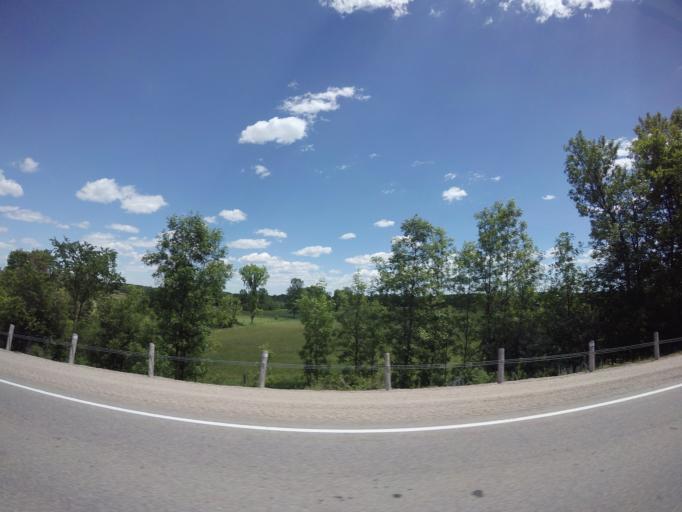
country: CA
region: Ontario
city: Carleton Place
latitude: 45.1228
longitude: -76.2112
